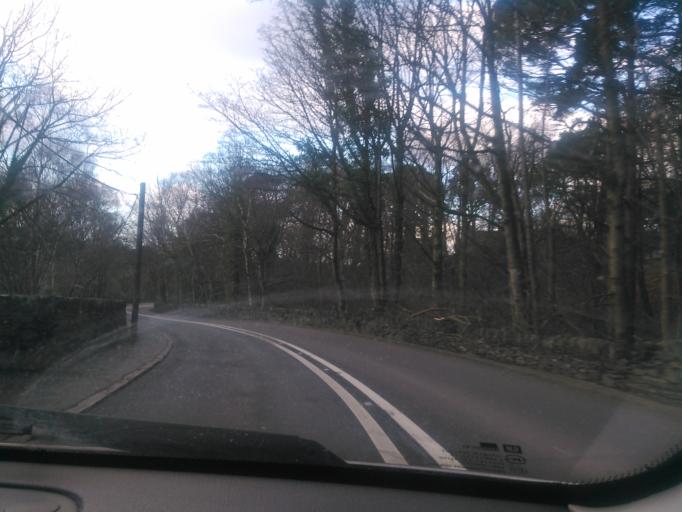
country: GB
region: Wales
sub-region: Gwynedd
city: Bethesda
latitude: 53.1695
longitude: -4.0562
